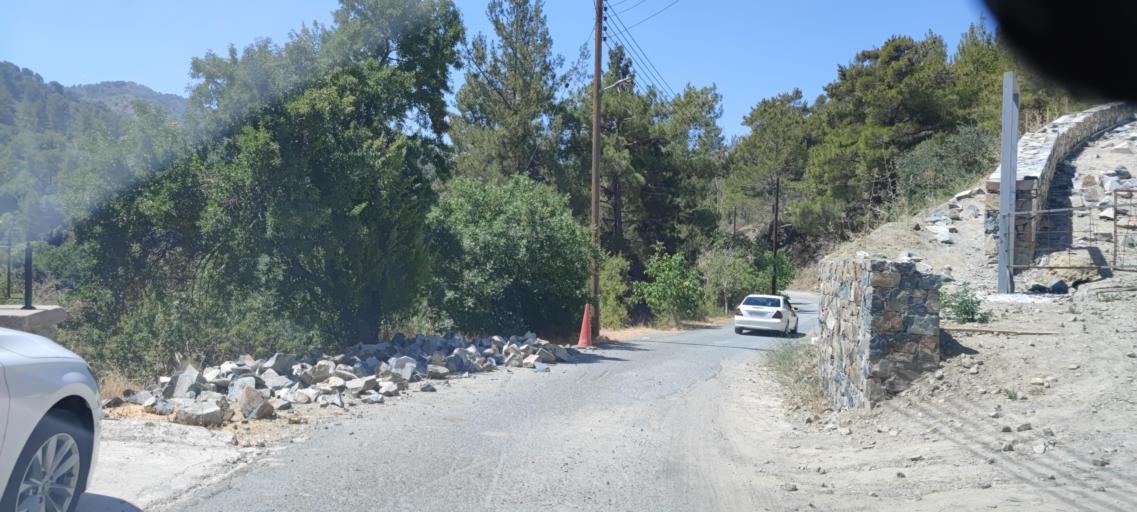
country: CY
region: Lefkosia
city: Kakopetria
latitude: 34.9300
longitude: 32.7943
